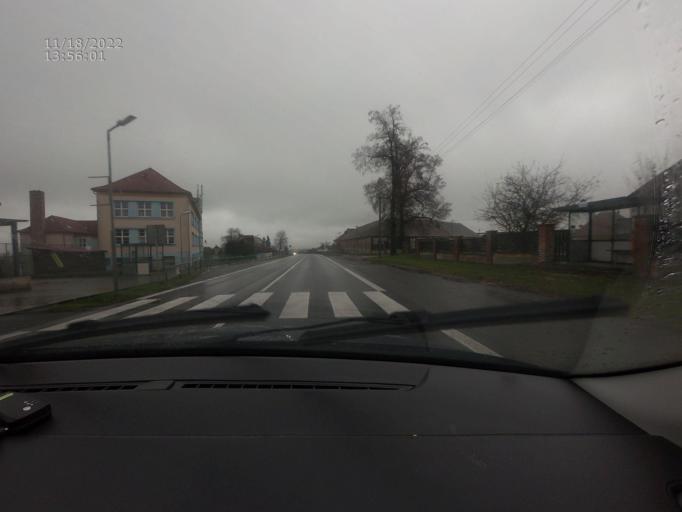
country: CZ
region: Jihocesky
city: Sedlice
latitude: 49.3739
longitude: 13.9418
